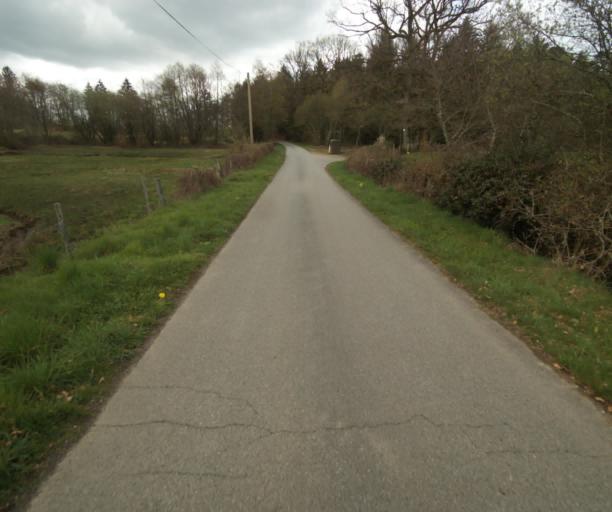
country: FR
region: Limousin
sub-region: Departement de la Correze
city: Laguenne
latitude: 45.2519
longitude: 1.8676
